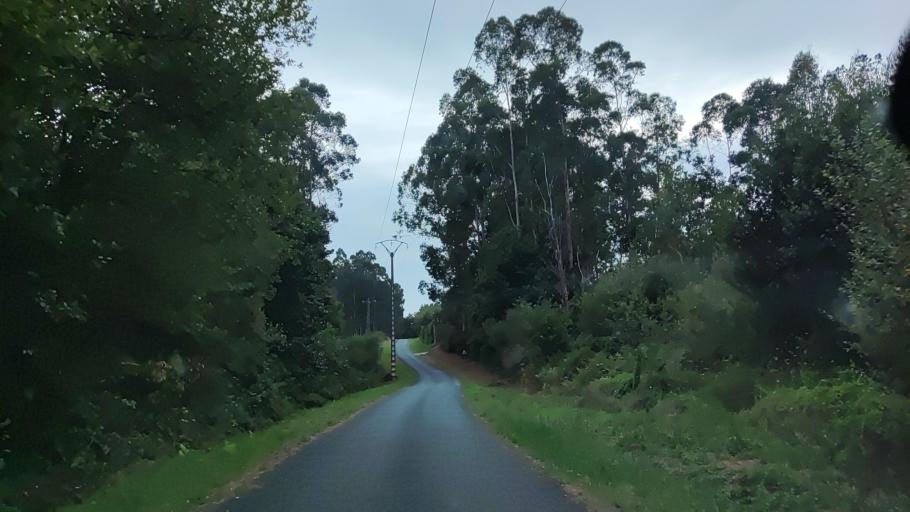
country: ES
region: Galicia
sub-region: Provincia da Coruna
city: Padron
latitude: 42.7215
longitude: -8.6783
